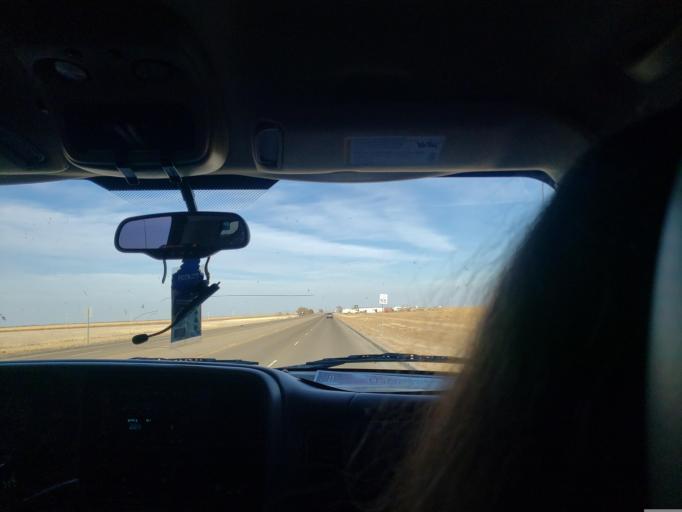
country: US
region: Oklahoma
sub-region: Texas County
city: Goodwell
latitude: 36.5064
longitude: -101.7727
